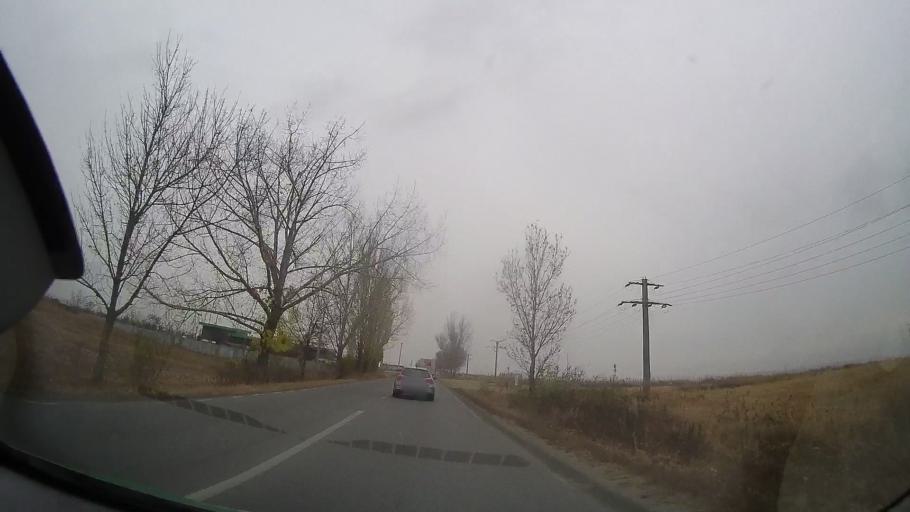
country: RO
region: Prahova
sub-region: Comuna Paulesti
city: Paulesti
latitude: 44.9820
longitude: 25.9854
